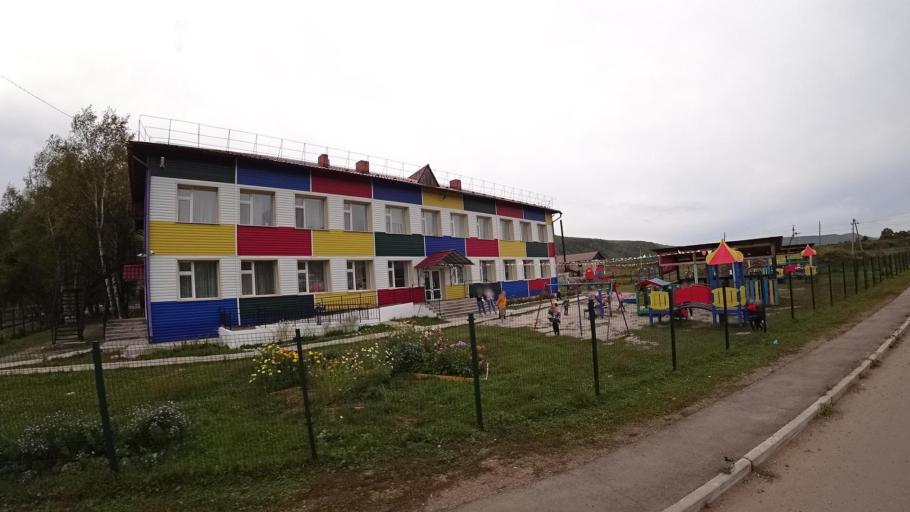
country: RU
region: Jewish Autonomous Oblast
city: Khingansk
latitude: 49.0283
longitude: 131.0493
